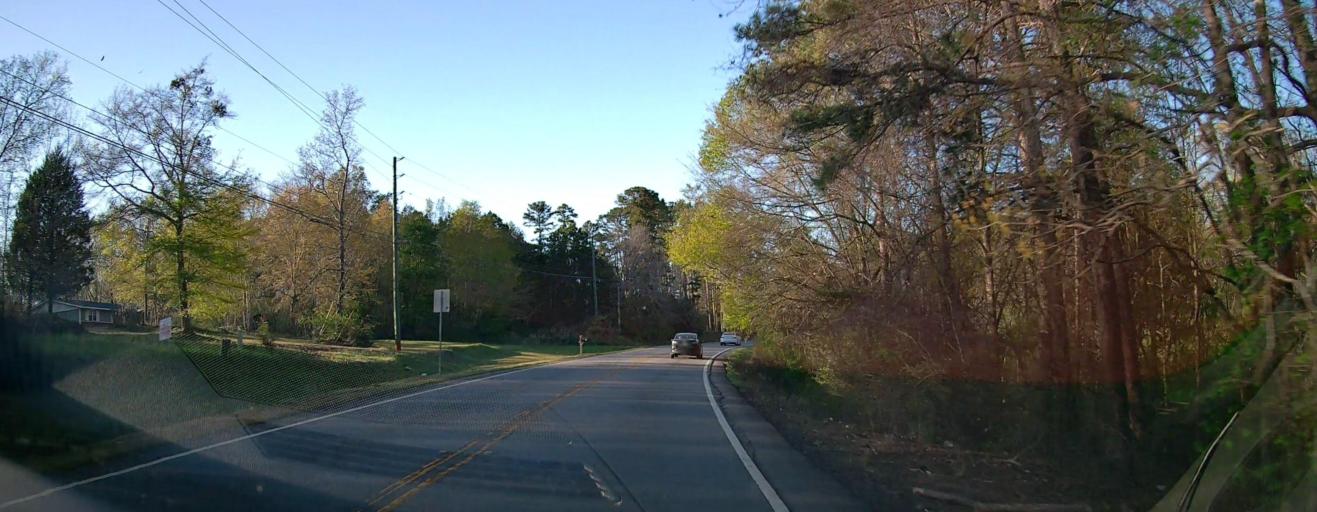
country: US
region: Georgia
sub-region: Newton County
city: Porterdale
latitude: 33.5385
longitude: -83.9176
